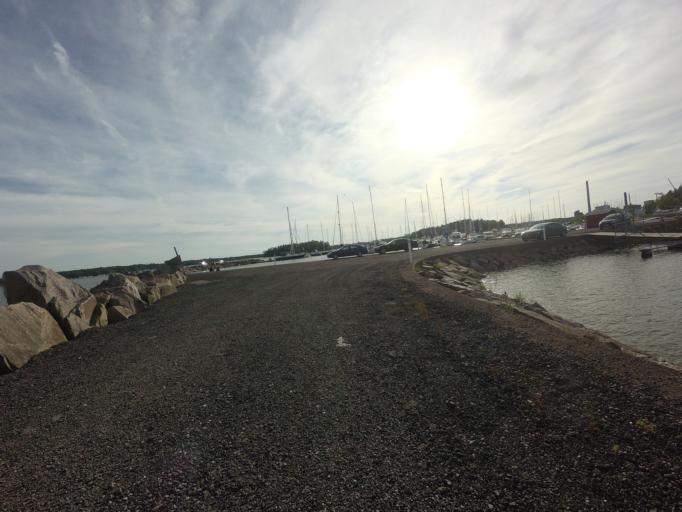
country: FI
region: Uusimaa
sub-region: Helsinki
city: Koukkuniemi
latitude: 60.1427
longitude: 24.7396
